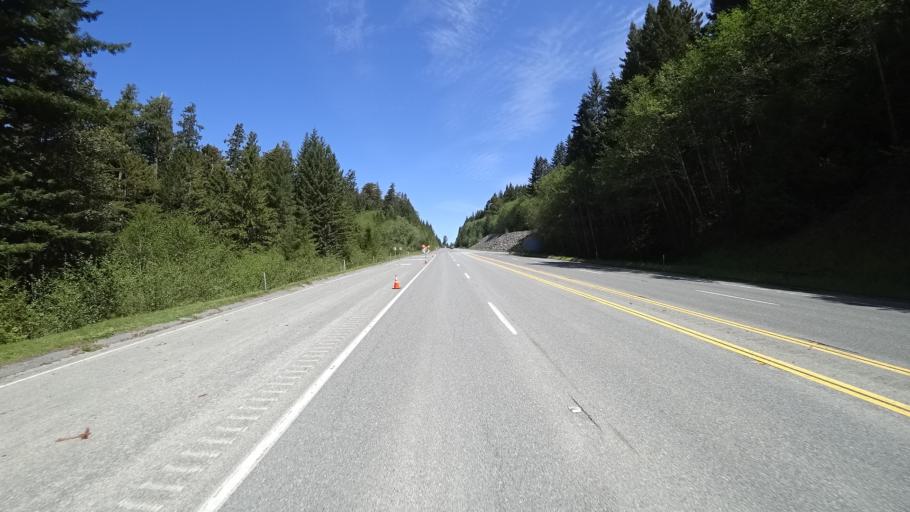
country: US
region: California
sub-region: Humboldt County
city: Westhaven-Moonstone
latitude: 41.3807
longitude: -123.9951
